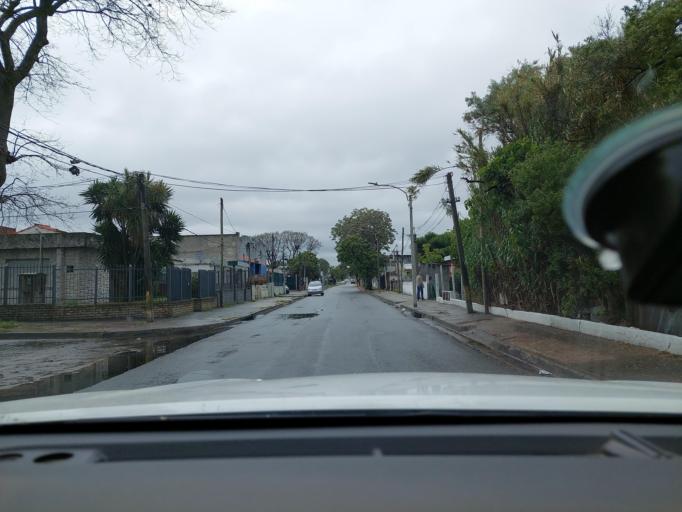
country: UY
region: Montevideo
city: Montevideo
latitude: -34.8634
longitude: -56.1457
